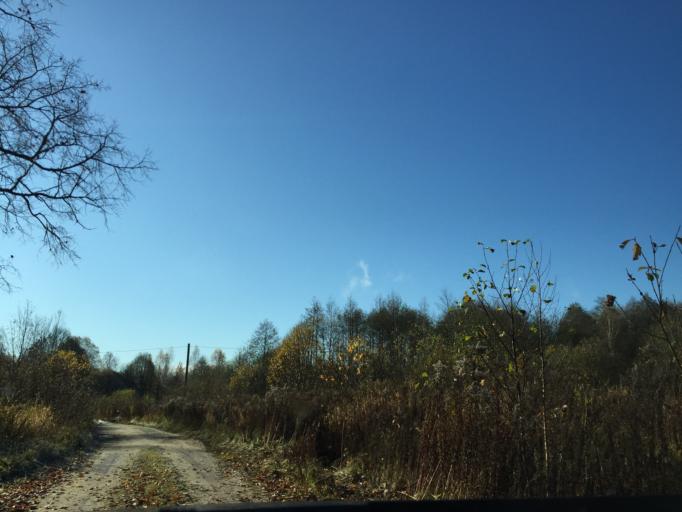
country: LV
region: Aizkraukles Rajons
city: Aizkraukle
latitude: 56.7104
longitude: 25.3000
